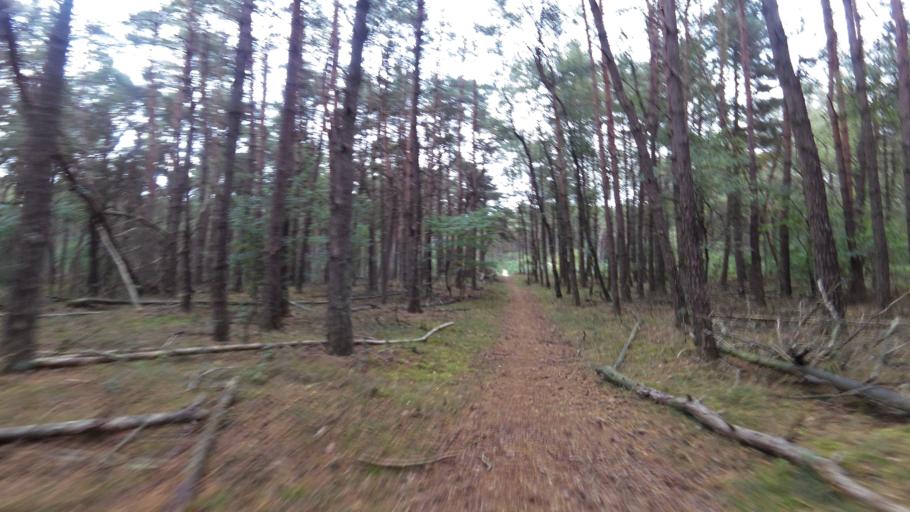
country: NL
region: Gelderland
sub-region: Gemeente Ede
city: Harskamp
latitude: 52.1545
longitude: 5.7485
